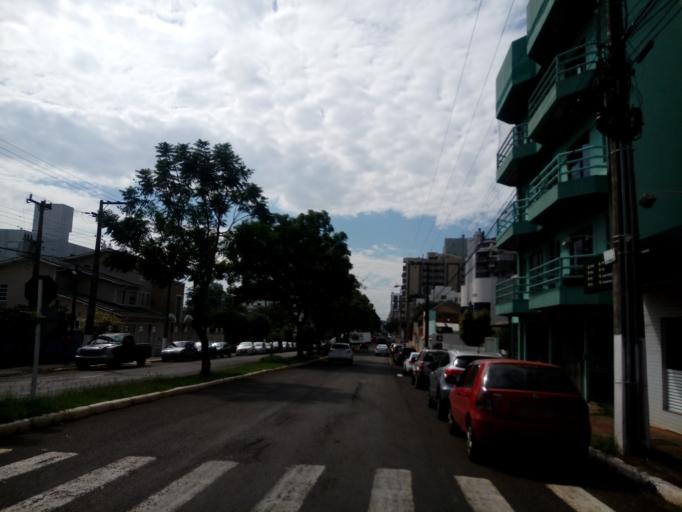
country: BR
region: Santa Catarina
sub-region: Chapeco
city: Chapeco
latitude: -27.1099
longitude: -52.6164
